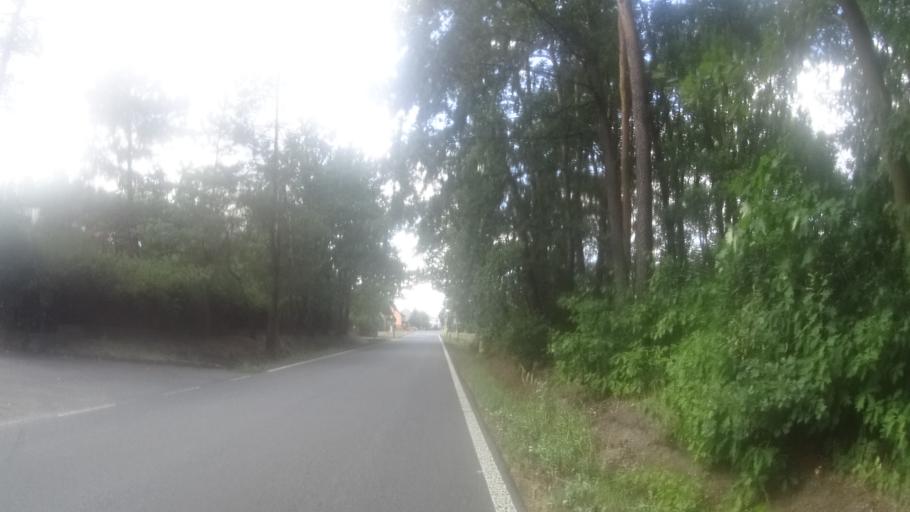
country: CZ
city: Borohradek
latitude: 50.0910
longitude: 16.1032
